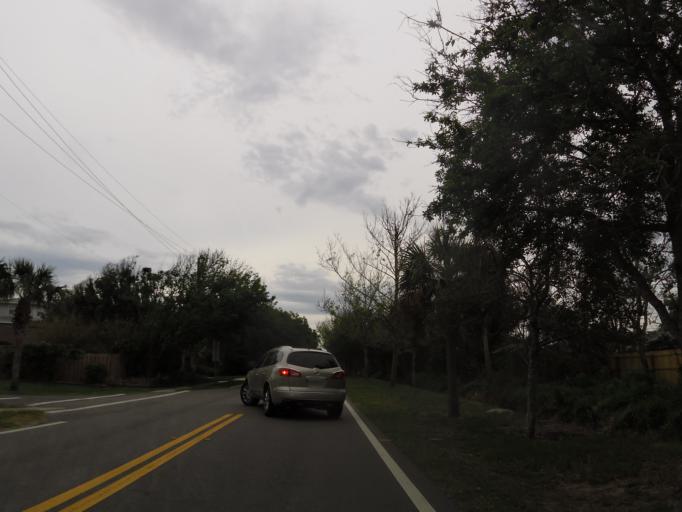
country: US
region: Florida
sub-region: Duval County
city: Atlantic Beach
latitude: 30.3431
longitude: -81.3992
